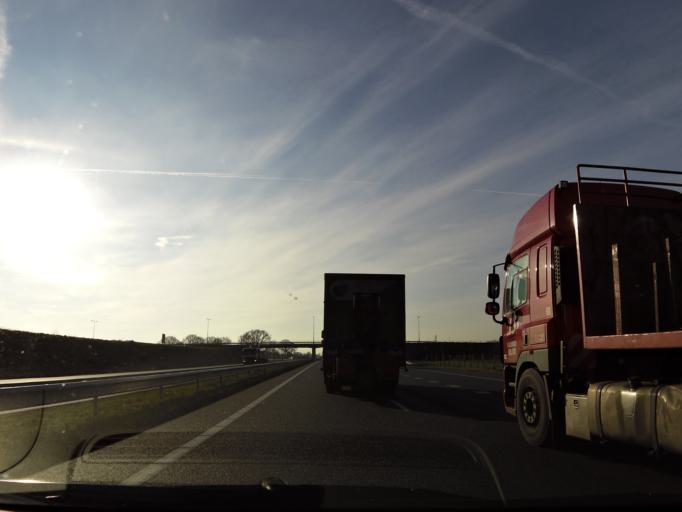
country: NL
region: Limburg
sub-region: Gemeente Venlo
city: Tegelen
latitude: 51.3189
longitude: 6.1365
